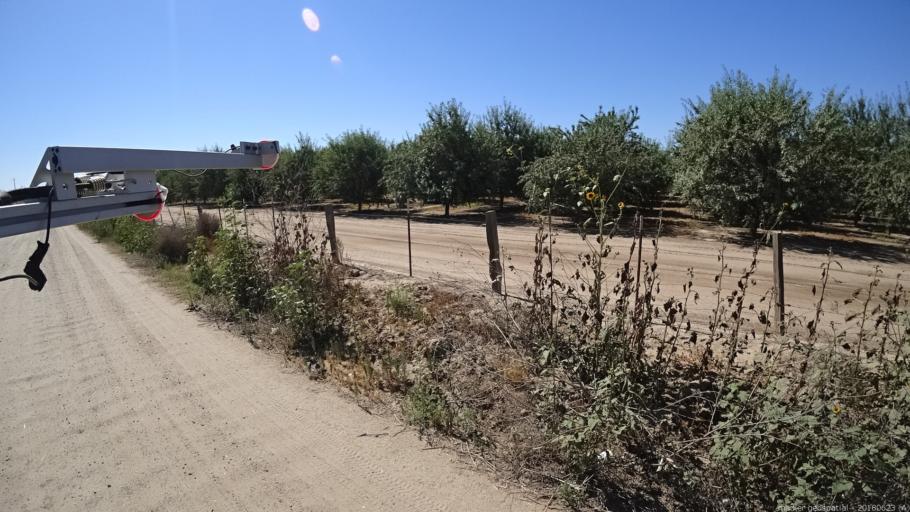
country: US
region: California
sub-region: Madera County
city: Parksdale
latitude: 36.9743
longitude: -120.0053
